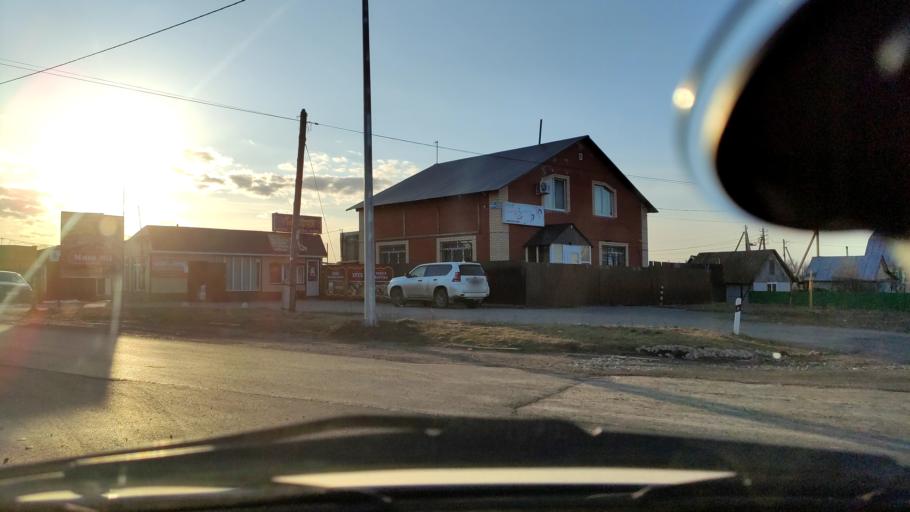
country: RU
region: Bashkortostan
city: Kabakovo
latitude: 54.6563
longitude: 56.1938
